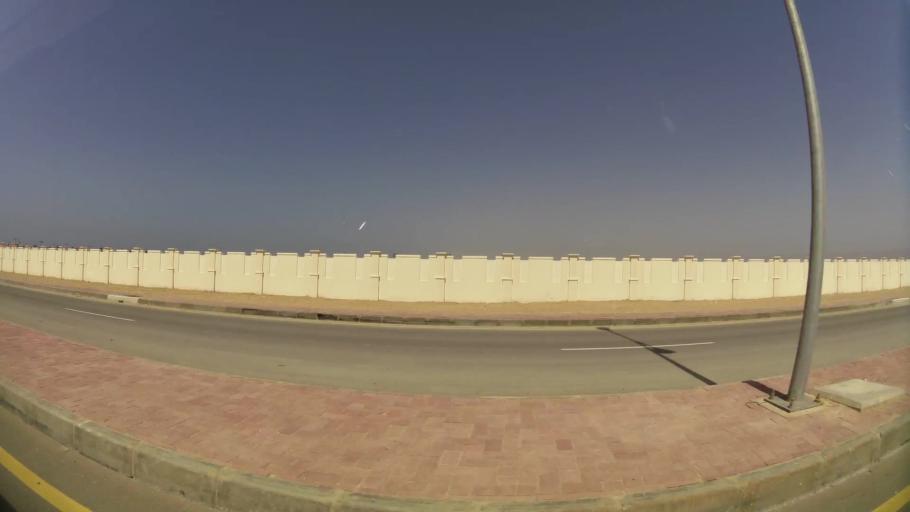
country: OM
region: Zufar
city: Salalah
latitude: 17.0326
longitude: 54.1349
